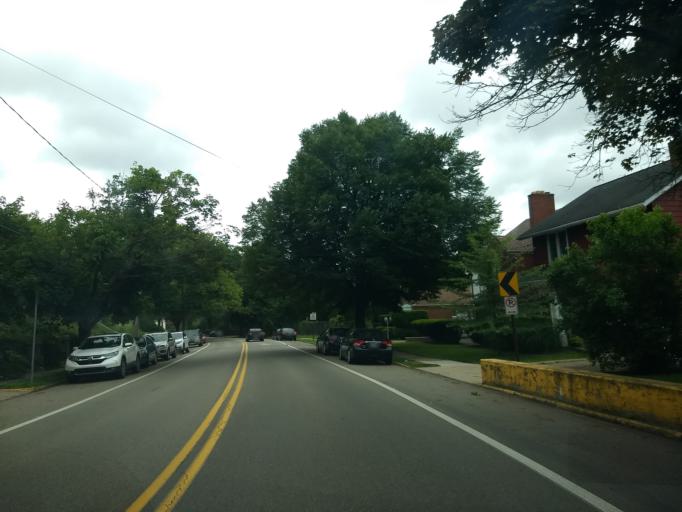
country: US
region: Pennsylvania
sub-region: Allegheny County
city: Homestead
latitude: 40.4179
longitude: -79.9232
